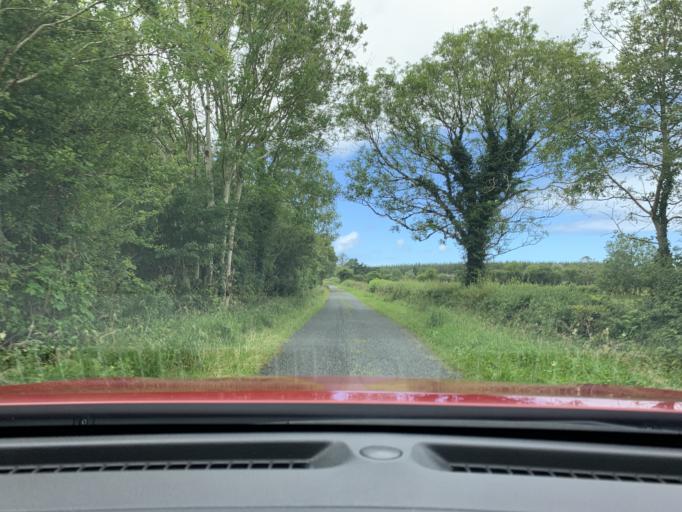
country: IE
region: Connaught
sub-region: Sligo
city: Sligo
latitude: 54.3316
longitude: -8.4888
